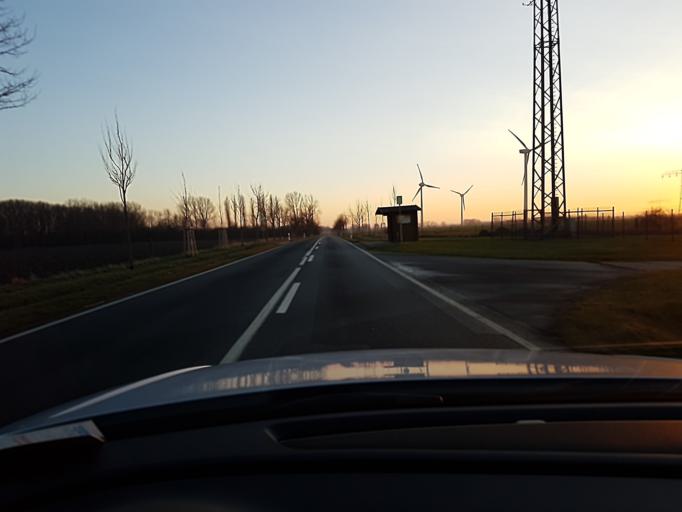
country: DE
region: Mecklenburg-Vorpommern
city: Wiek
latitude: 54.6014
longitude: 13.2911
